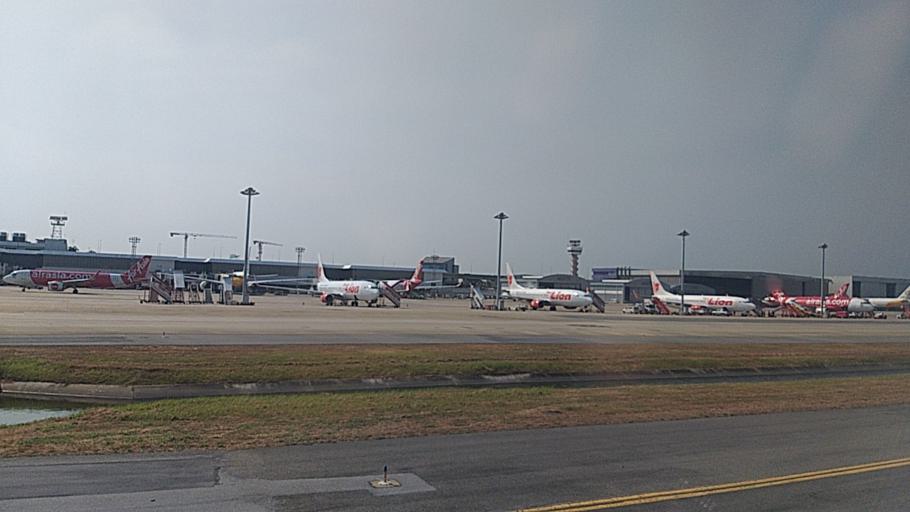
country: TH
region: Bangkok
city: Don Mueang
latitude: 13.9213
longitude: 100.6077
